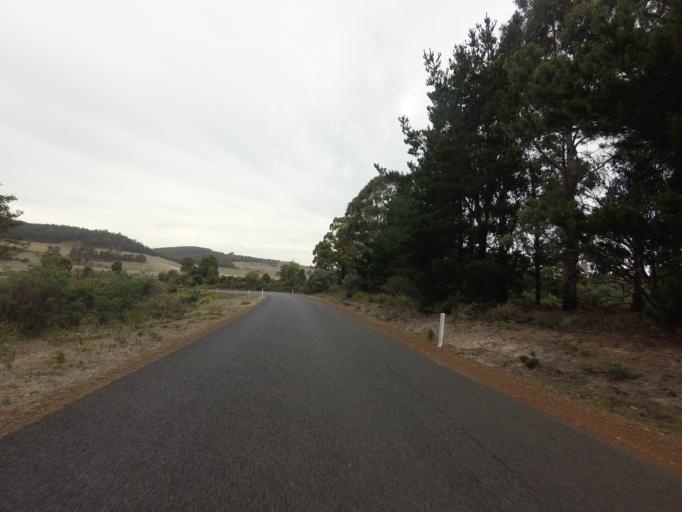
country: AU
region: Tasmania
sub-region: Sorell
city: Sorell
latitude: -42.5673
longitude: 147.5715
